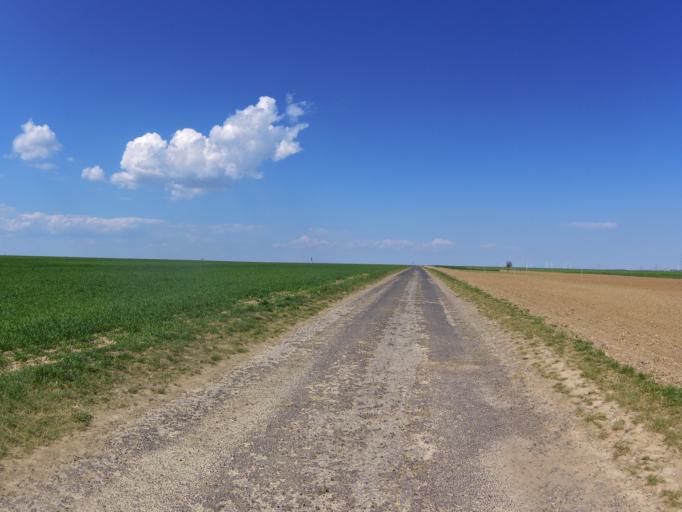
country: DE
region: Bavaria
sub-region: Regierungsbezirk Unterfranken
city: Oberpleichfeld
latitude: 49.8501
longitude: 10.0877
